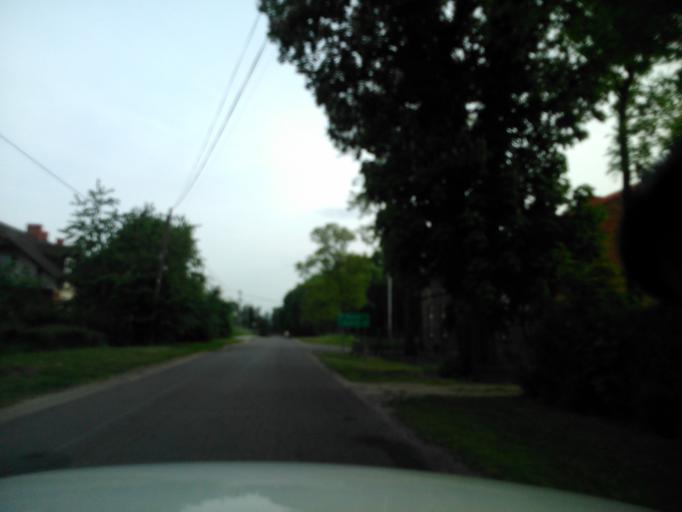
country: PL
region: Kujawsko-Pomorskie
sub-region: Powiat golubsko-dobrzynski
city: Kowalewo Pomorskie
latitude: 53.1188
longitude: 18.9131
